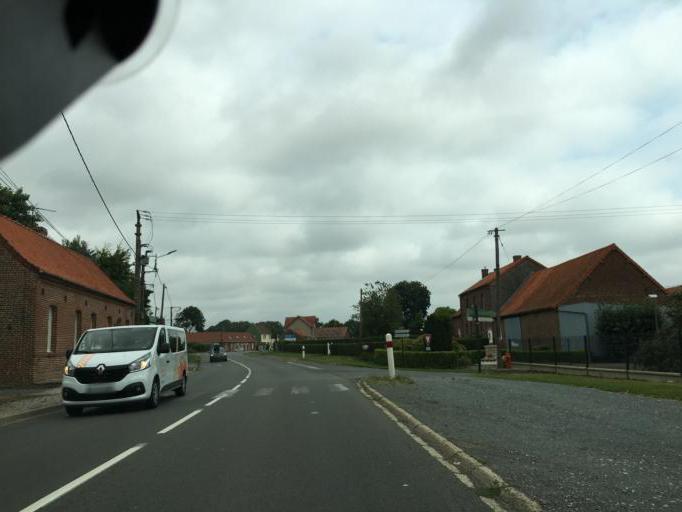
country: FR
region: Nord-Pas-de-Calais
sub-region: Departement du Pas-de-Calais
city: Saint-Pol-sur-Ternoise
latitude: 50.4115
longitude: 2.3778
